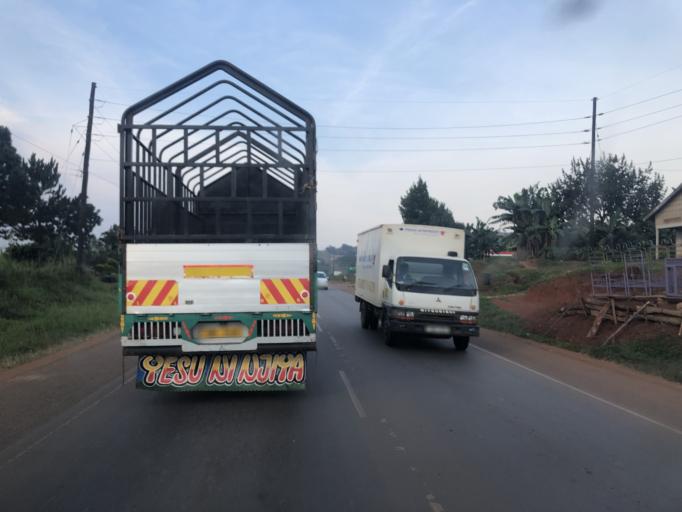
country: UG
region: Central Region
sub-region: Mpigi District
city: Mpigi
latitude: 0.2494
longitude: 32.3882
